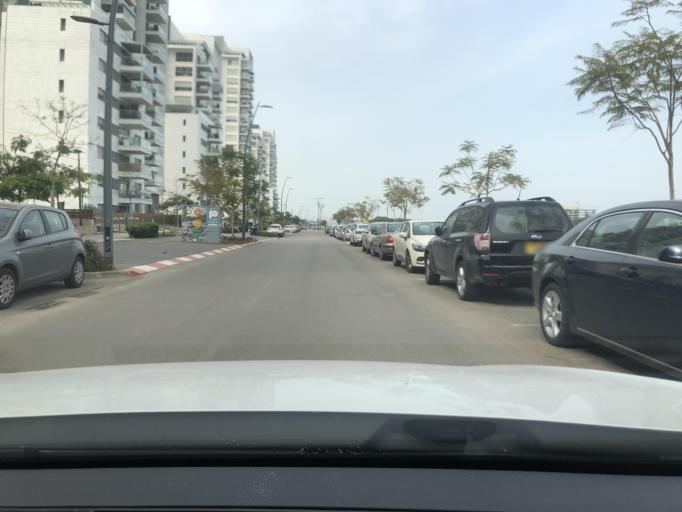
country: IL
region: Central District
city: Rosh Ha'Ayin
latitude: 32.1069
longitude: 34.9479
